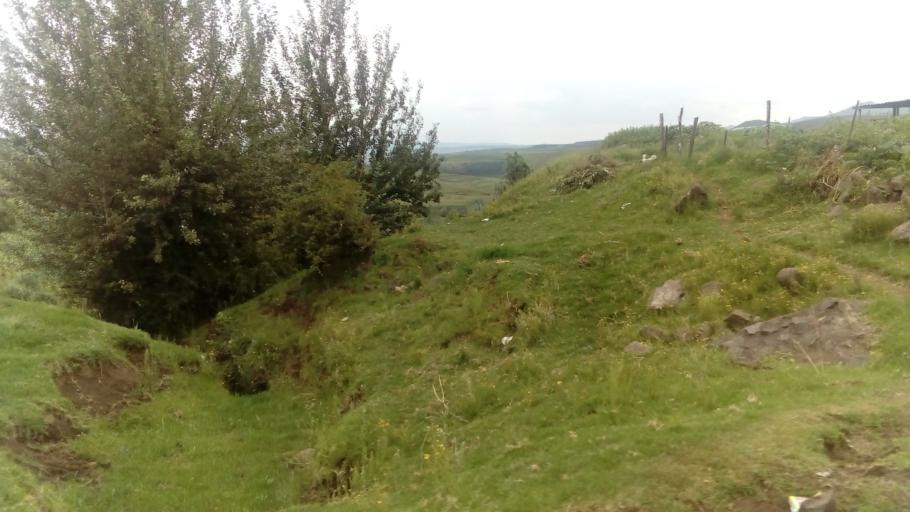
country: LS
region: Butha-Buthe
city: Butha-Buthe
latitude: -29.0339
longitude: 28.2650
